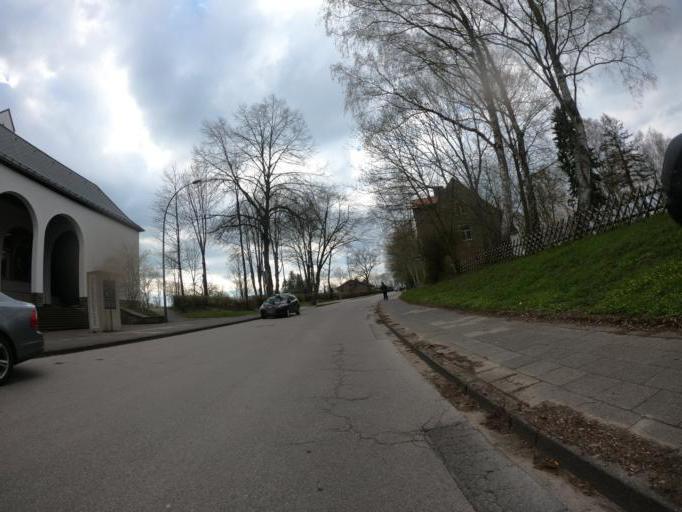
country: DE
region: North Rhine-Westphalia
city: Stolberg
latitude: 50.7301
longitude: 6.1680
